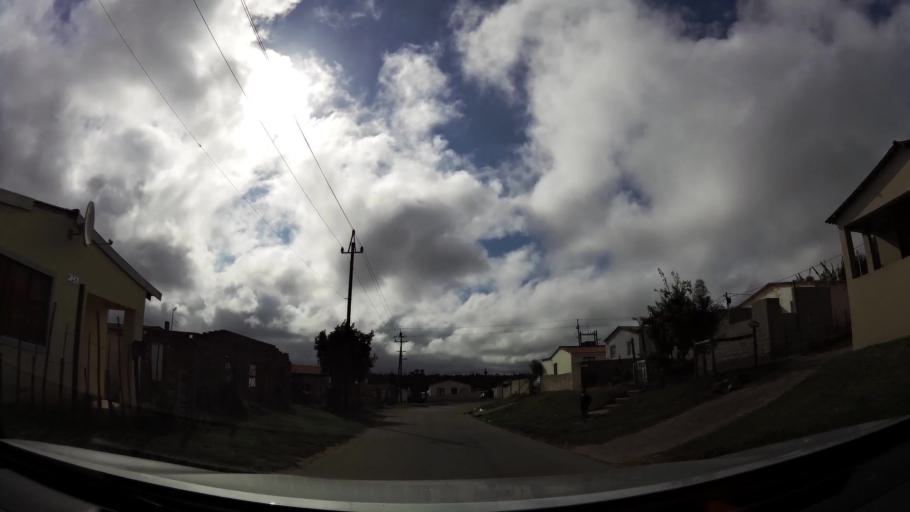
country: ZA
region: Western Cape
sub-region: Eden District Municipality
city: Plettenberg Bay
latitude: -34.0482
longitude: 23.3219
